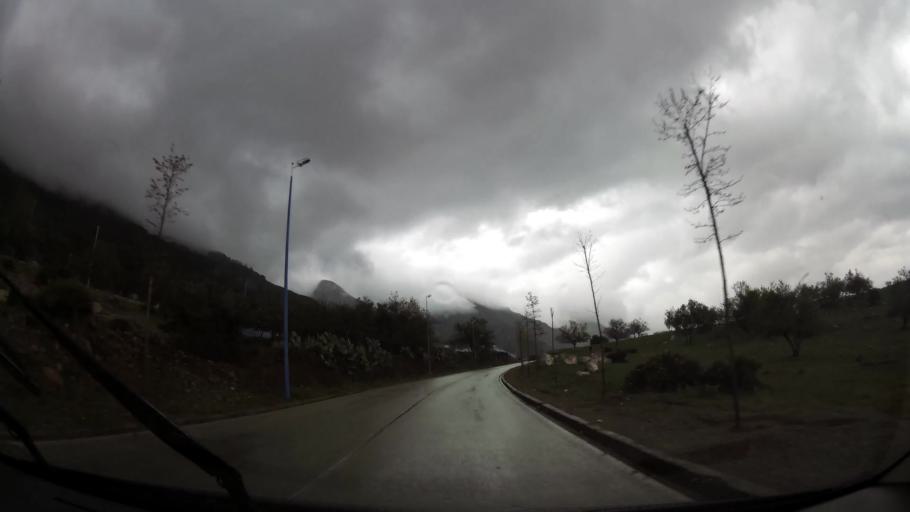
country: MA
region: Tanger-Tetouan
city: Chefchaouene
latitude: 35.1751
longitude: -5.2683
